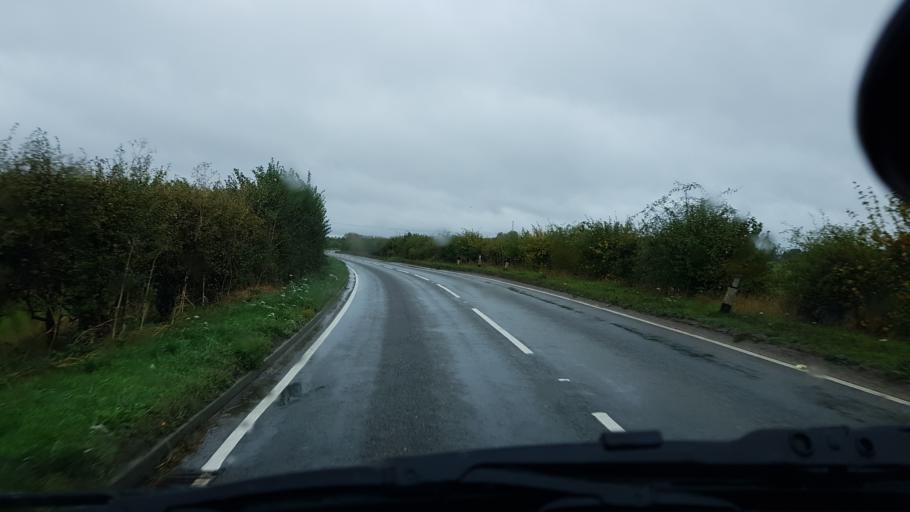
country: GB
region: England
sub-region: Oxfordshire
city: Frilford
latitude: 51.6755
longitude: -1.3877
